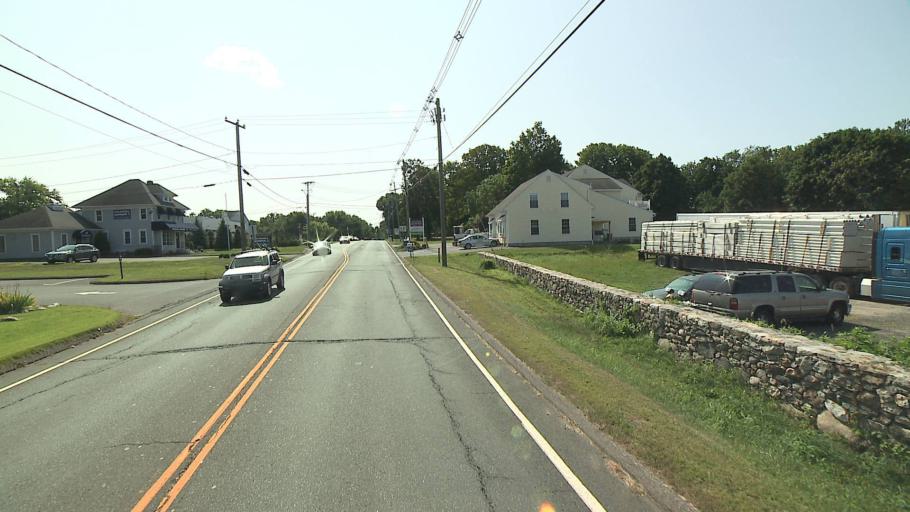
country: US
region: Connecticut
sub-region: Fairfield County
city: Newtown
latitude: 41.4026
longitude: -73.2979
